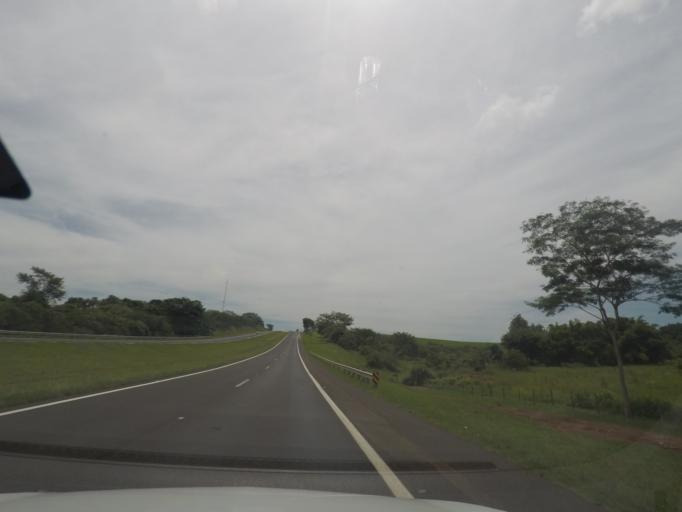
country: BR
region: Sao Paulo
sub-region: Bebedouro
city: Bebedouro
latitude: -20.9717
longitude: -48.4397
